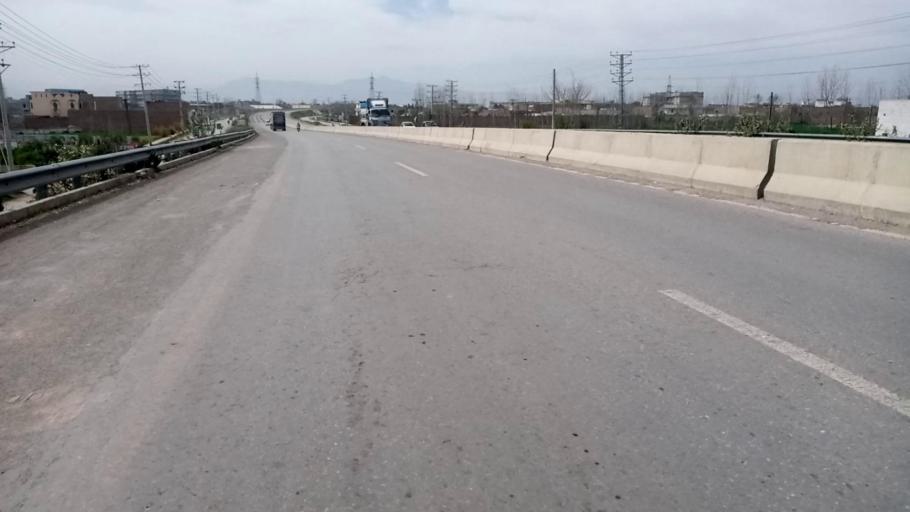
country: PK
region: Khyber Pakhtunkhwa
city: Peshawar
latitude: 34.0379
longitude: 71.6282
